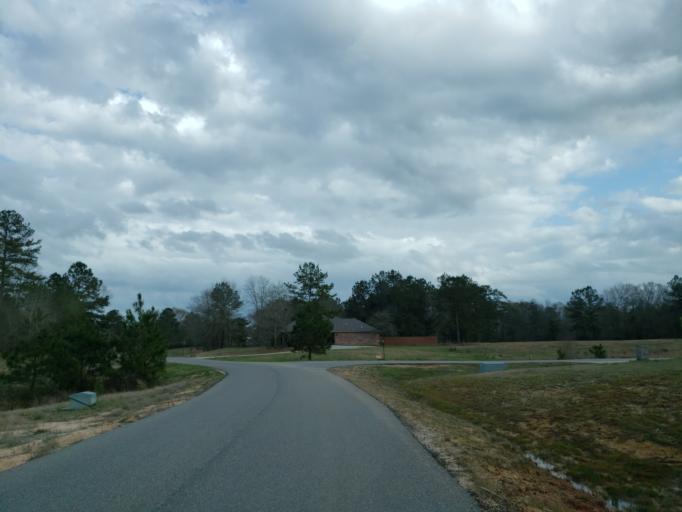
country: US
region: Mississippi
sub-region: Jones County
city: Ellisville
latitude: 31.5629
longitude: -89.2483
